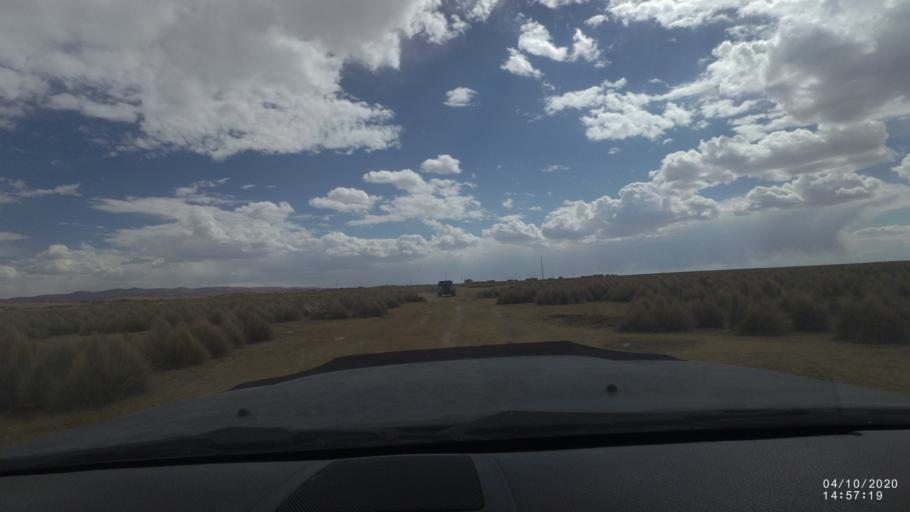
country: BO
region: Oruro
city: Poopo
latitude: -18.6853
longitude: -67.5184
